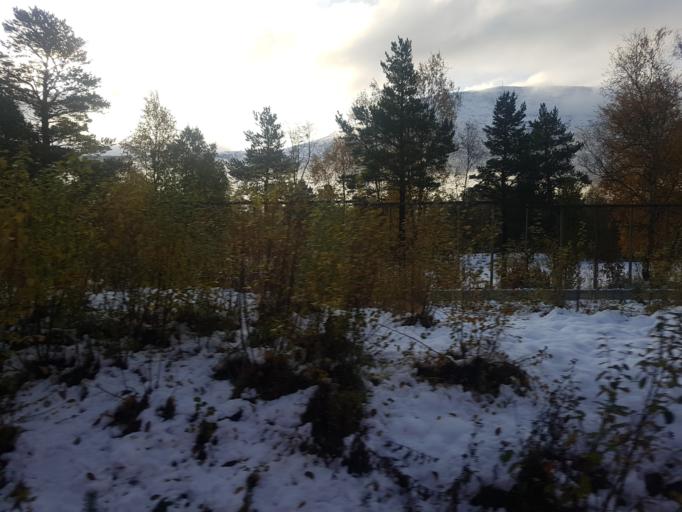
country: NO
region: Sor-Trondelag
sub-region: Oppdal
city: Oppdal
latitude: 62.6011
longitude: 9.7090
